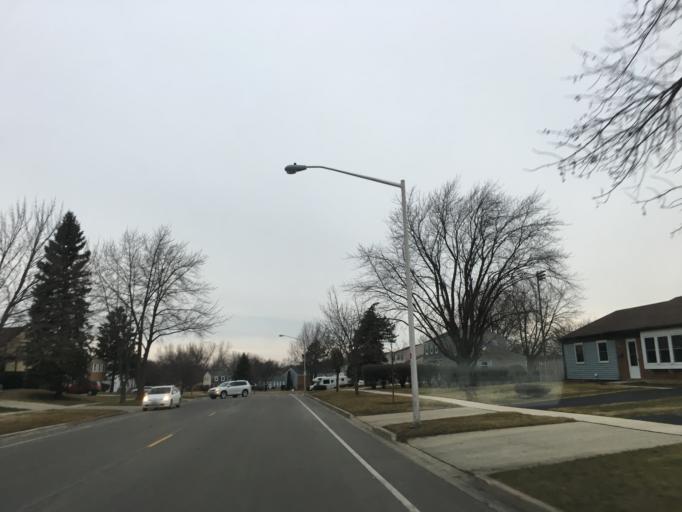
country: US
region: Illinois
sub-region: Cook County
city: Schaumburg
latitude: 42.0273
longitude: -88.1100
